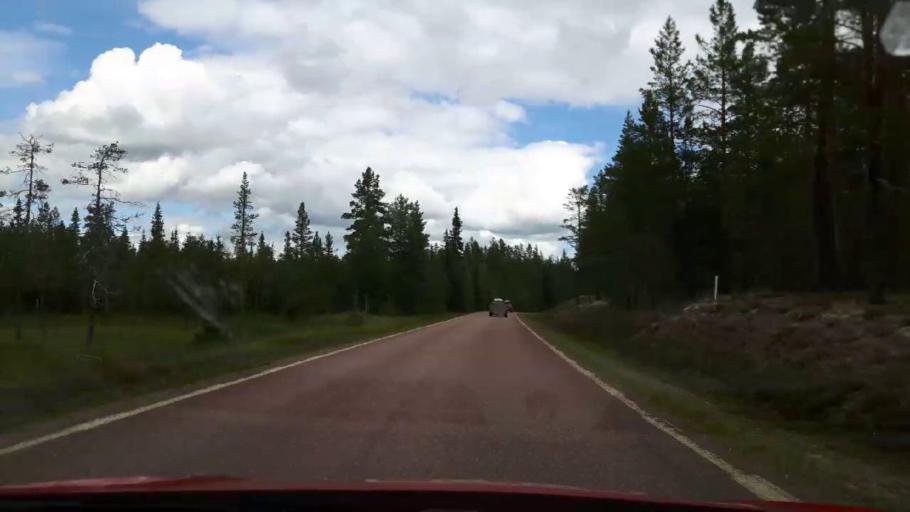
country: NO
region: Hedmark
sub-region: Trysil
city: Innbygda
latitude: 61.8597
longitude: 12.9472
